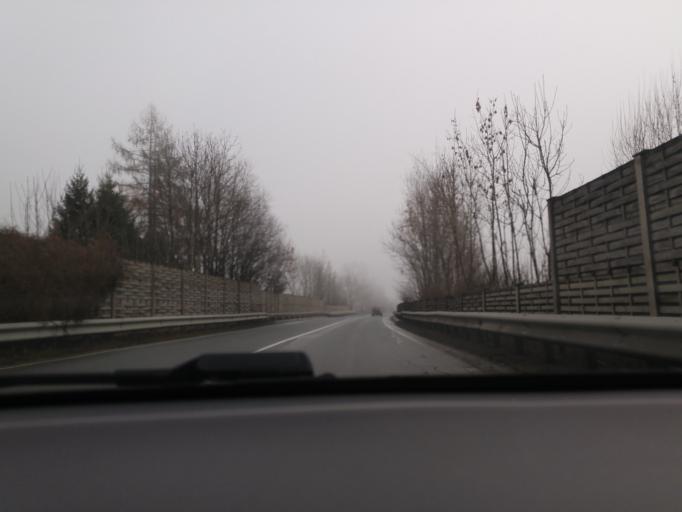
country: AT
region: Salzburg
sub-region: Politischer Bezirk Zell am See
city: Bruck an der Grossglocknerstrasse
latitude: 47.2801
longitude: 12.8298
